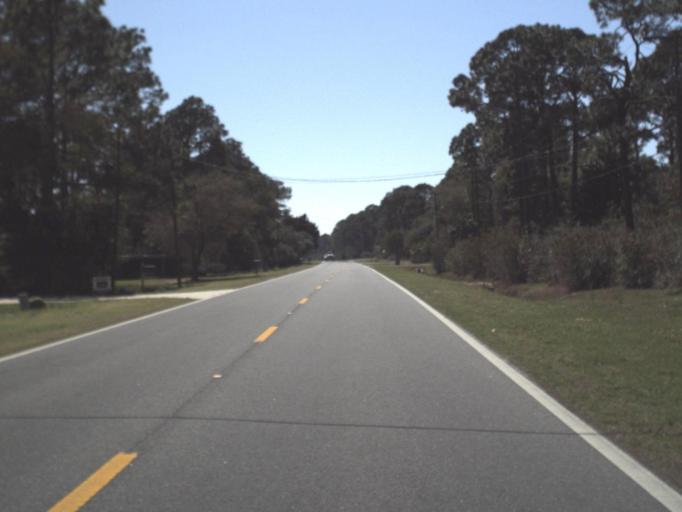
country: US
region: Florida
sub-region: Franklin County
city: Carrabelle
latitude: 29.8777
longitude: -84.6016
